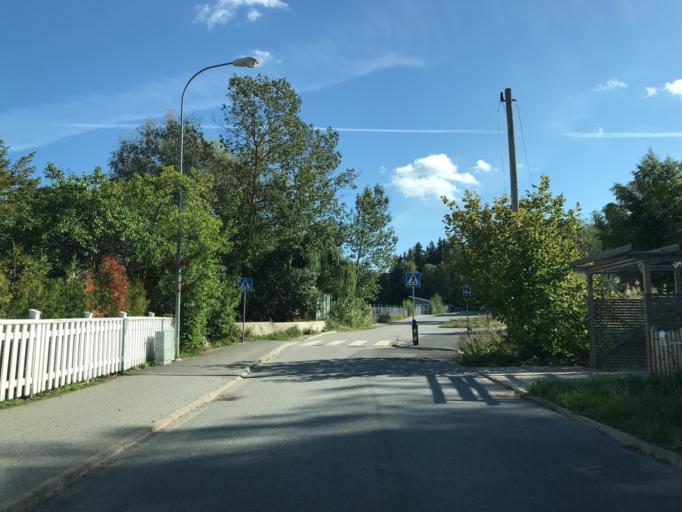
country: SE
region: Stockholm
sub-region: Sollentuna Kommun
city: Sollentuna
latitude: 59.4132
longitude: 17.9846
